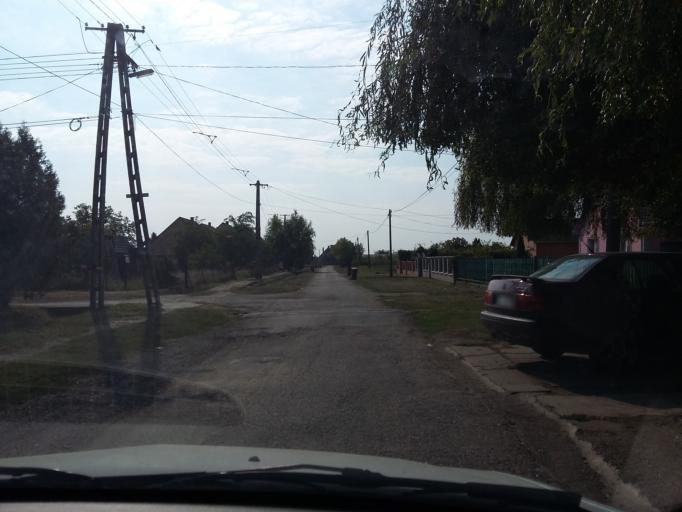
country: HU
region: Borsod-Abauj-Zemplen
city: Bekecs
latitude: 48.1512
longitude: 21.1784
